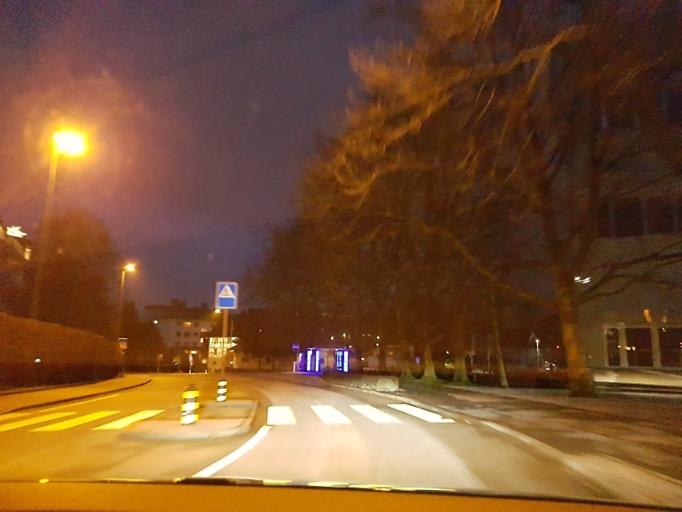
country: CH
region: Zurich
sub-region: Bezirk Horgen
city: Ruschlikon
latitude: 47.3073
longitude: 8.5480
